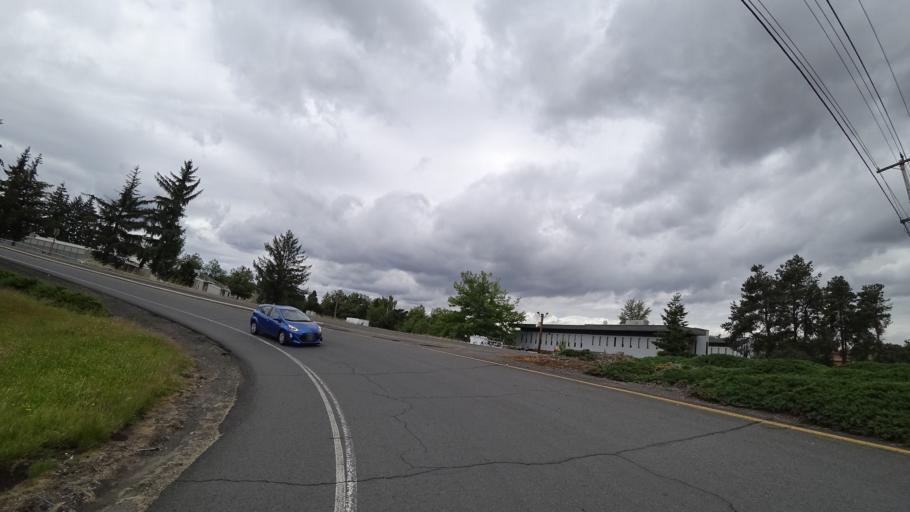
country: US
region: Oregon
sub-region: Multnomah County
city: Lents
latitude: 45.5660
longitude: -122.5782
